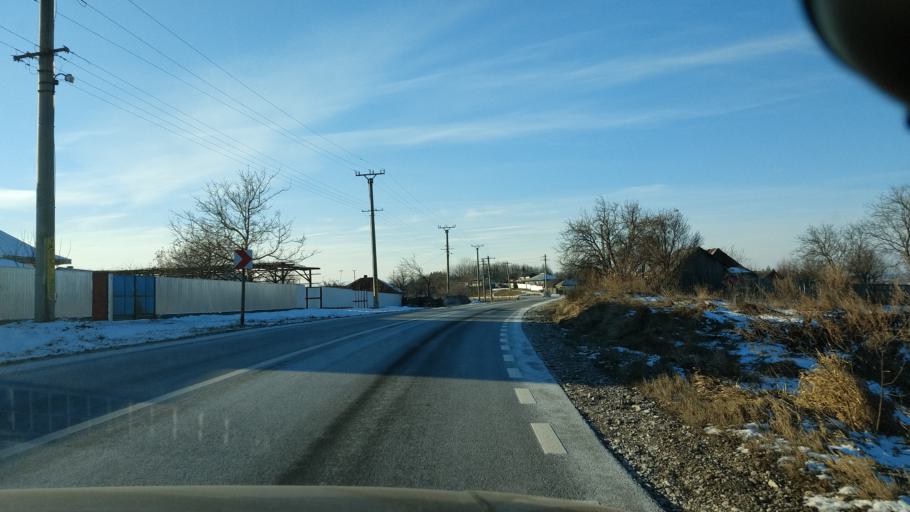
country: RO
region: Bacau
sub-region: Comuna Luizi-Calugara
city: Luizi-Calugara
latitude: 46.4921
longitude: 26.7845
